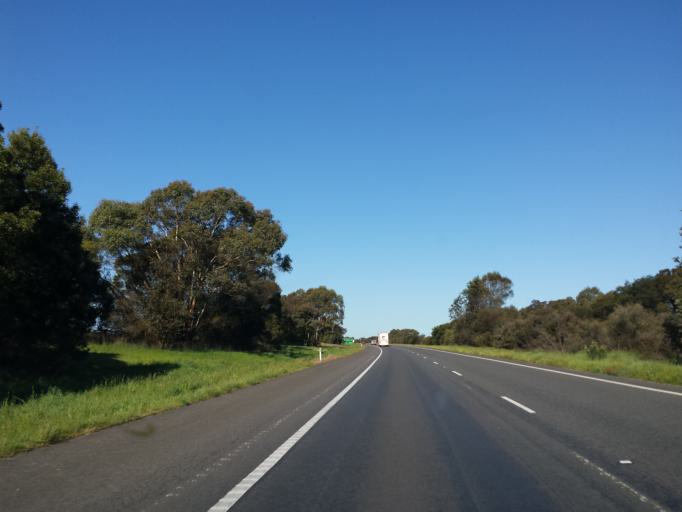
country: AU
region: Victoria
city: Brown Hill
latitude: -37.5500
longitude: 144.0352
